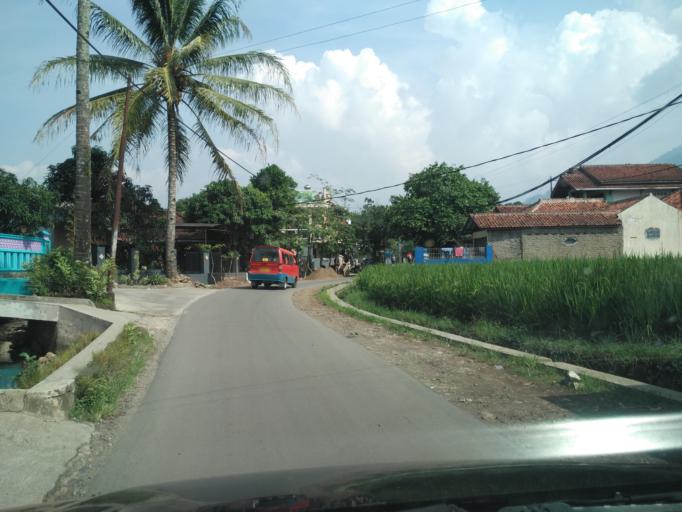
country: ID
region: West Java
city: Ciranjang-hilir
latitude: -6.7962
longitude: 107.1585
